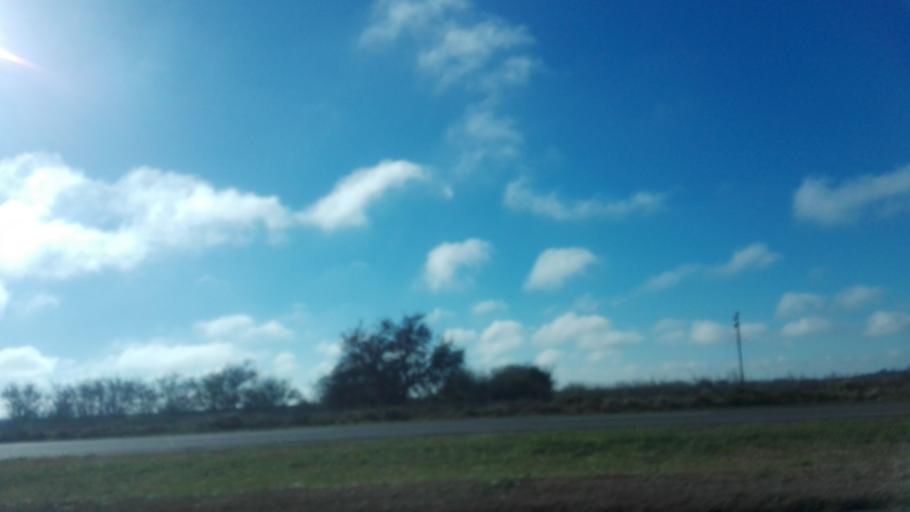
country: AR
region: Buenos Aires
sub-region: Partido de Chascomus
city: Chascomus
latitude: -35.8195
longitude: -57.9161
